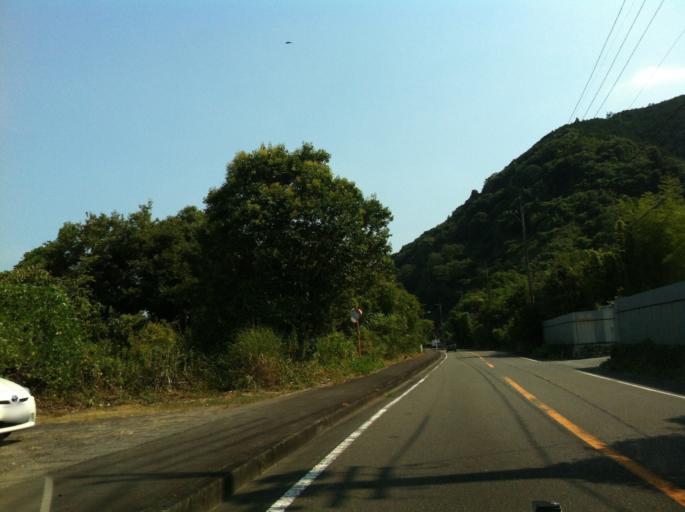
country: JP
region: Shizuoka
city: Shizuoka-shi
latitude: 35.0576
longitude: 138.3637
